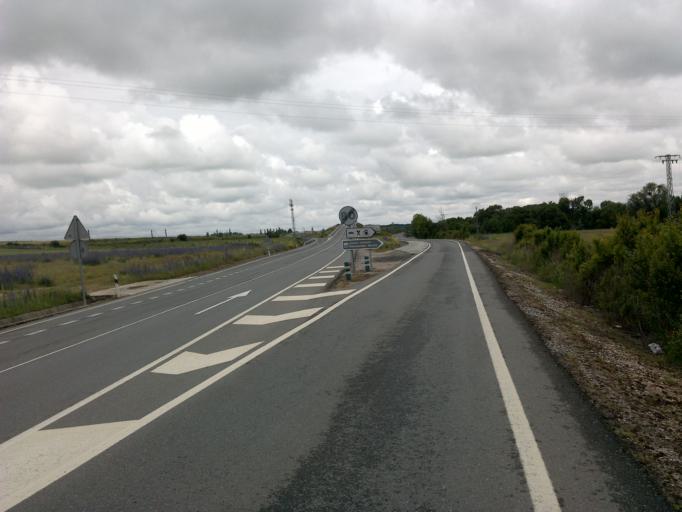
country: ES
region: Castille and Leon
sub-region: Provincia de Segovia
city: Hontanares de Eresma
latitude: 40.9527
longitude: -4.1804
